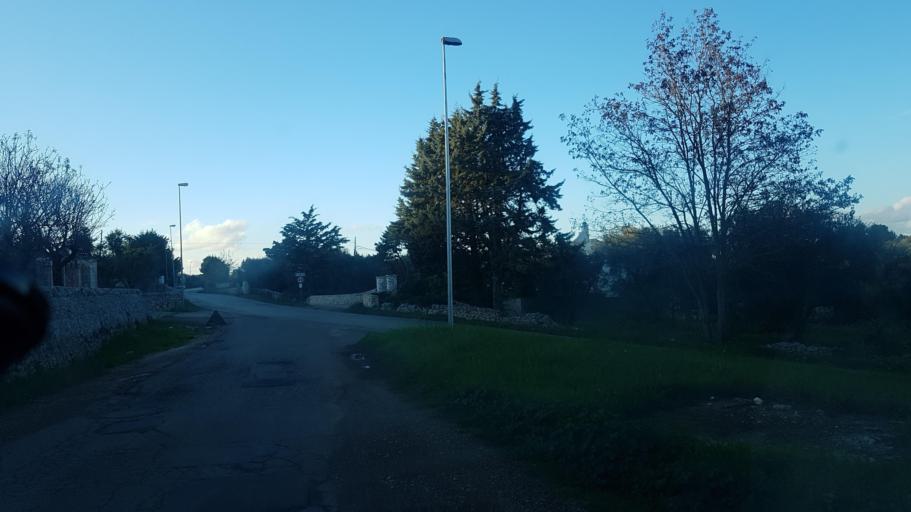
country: IT
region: Apulia
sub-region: Provincia di Brindisi
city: Ostuni
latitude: 40.7059
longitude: 17.5329
